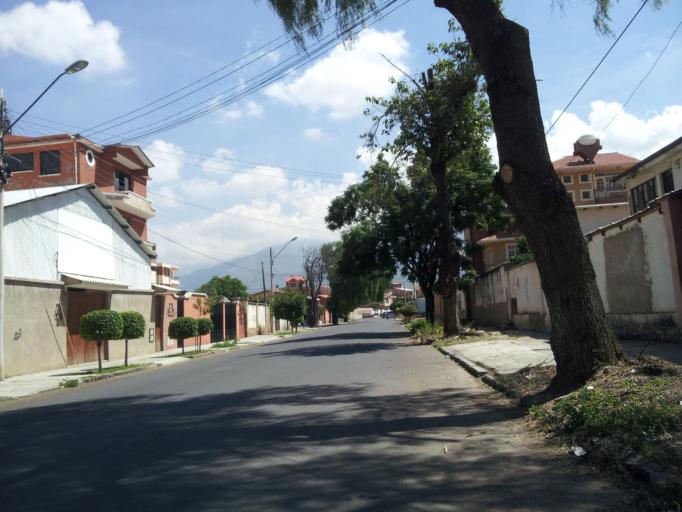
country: BO
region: Cochabamba
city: Cochabamba
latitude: -17.3896
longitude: -66.1738
